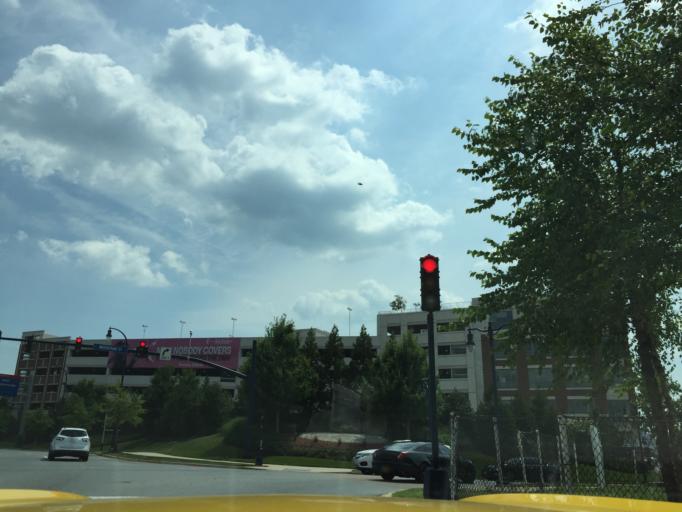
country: US
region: Maryland
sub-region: Prince George's County
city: Forest Heights
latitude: 38.7866
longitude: -77.0147
